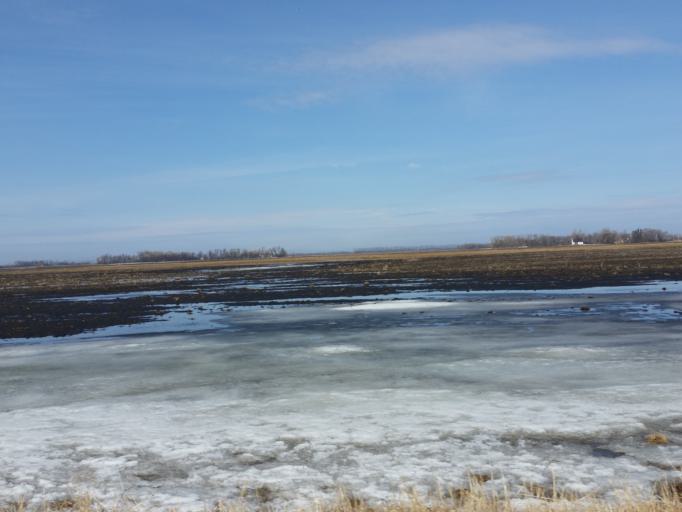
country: US
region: North Dakota
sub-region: Walsh County
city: Grafton
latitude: 48.4414
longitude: -97.4134
